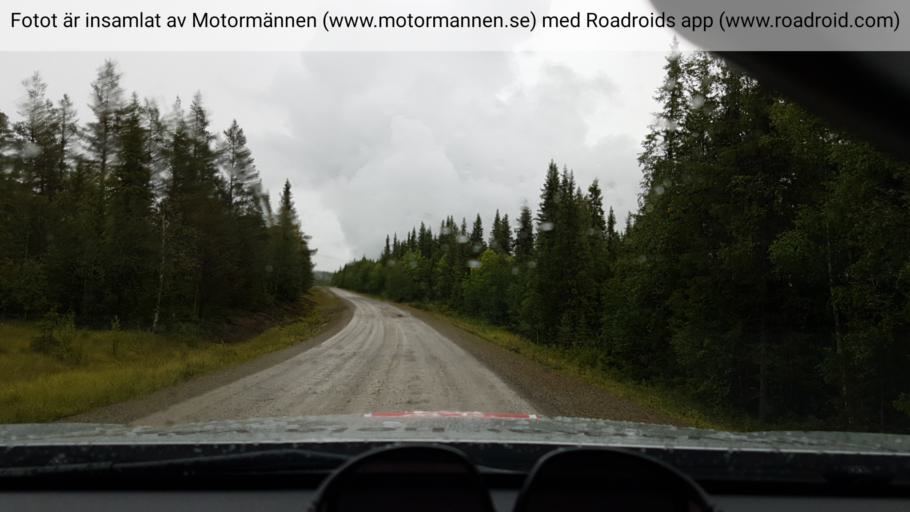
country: SE
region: Vaesterbotten
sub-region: Asele Kommun
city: Insjon
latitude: 64.7998
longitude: 17.5740
